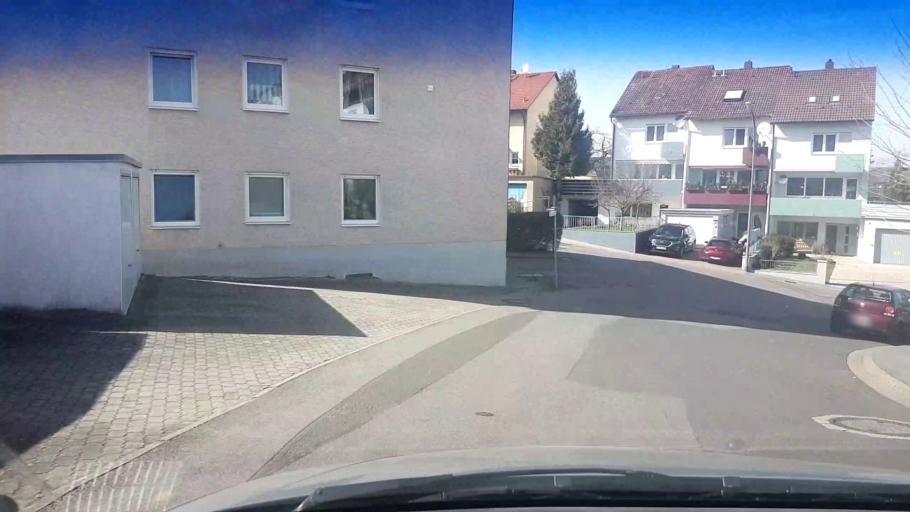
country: DE
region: Bavaria
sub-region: Upper Franconia
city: Bischberg
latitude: 49.9141
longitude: 10.8188
